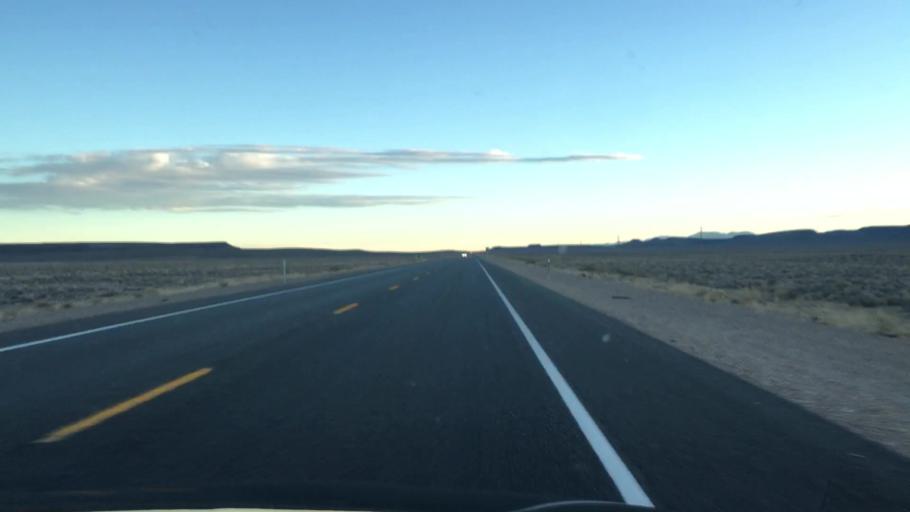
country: US
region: Nevada
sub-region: Esmeralda County
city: Goldfield
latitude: 37.4462
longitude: -117.1668
